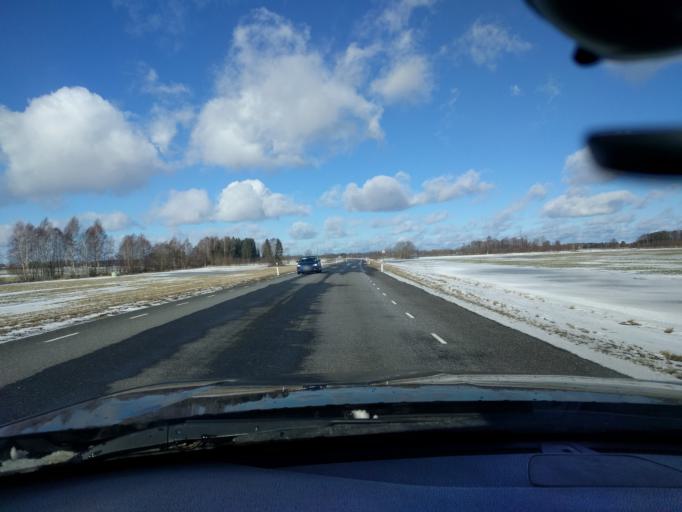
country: EE
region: Harju
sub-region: Anija vald
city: Kehra
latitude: 59.2446
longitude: 25.3541
